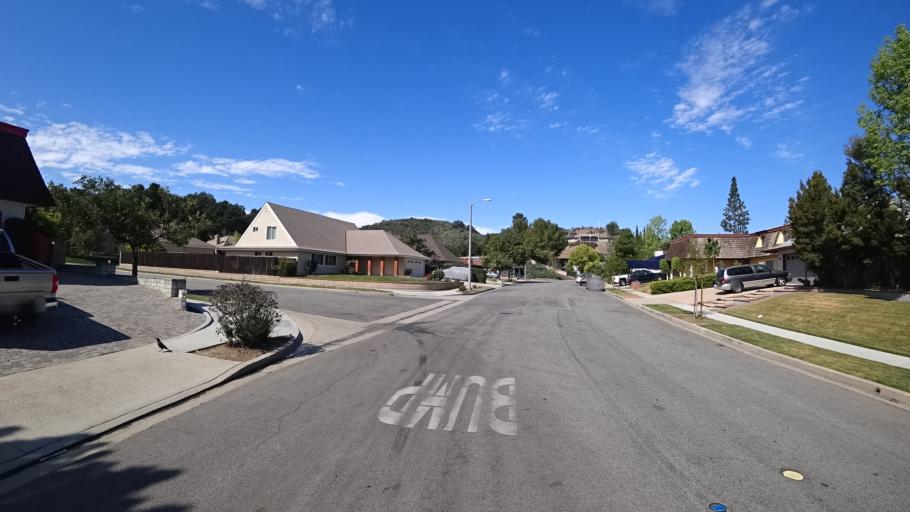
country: US
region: California
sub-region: Ventura County
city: Casa Conejo
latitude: 34.1772
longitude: -118.9272
